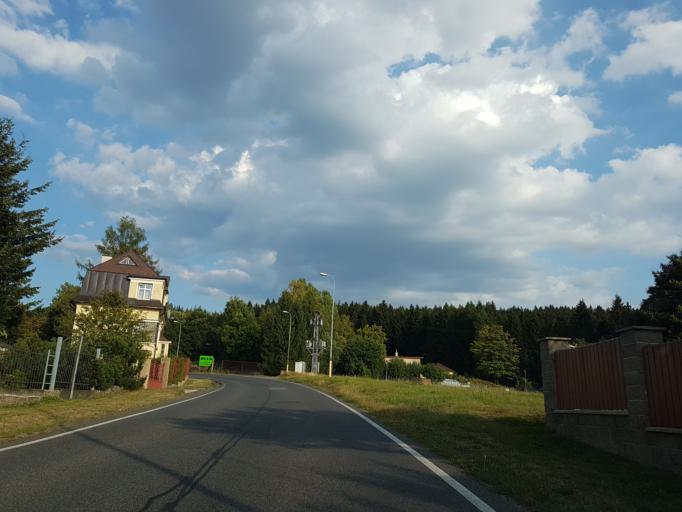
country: CZ
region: Liberecky
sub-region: Okres Jablonec nad Nisou
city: Jablonec nad Nisou
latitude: 50.7092
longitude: 15.1923
